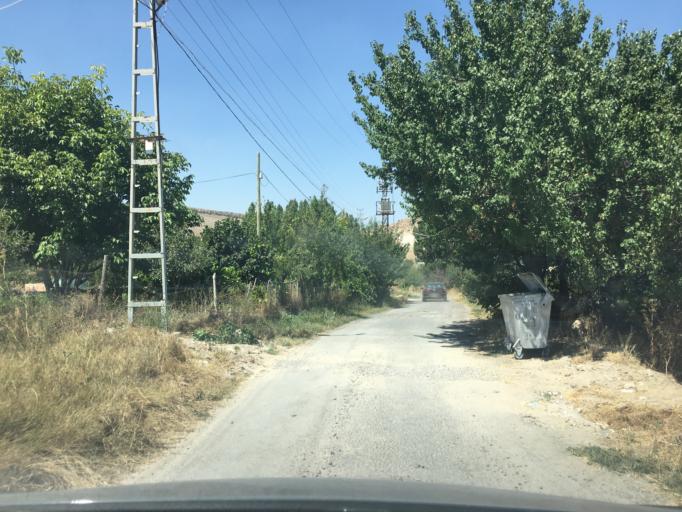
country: TR
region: Nevsehir
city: Urgub
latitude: 38.4686
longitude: 34.9616
